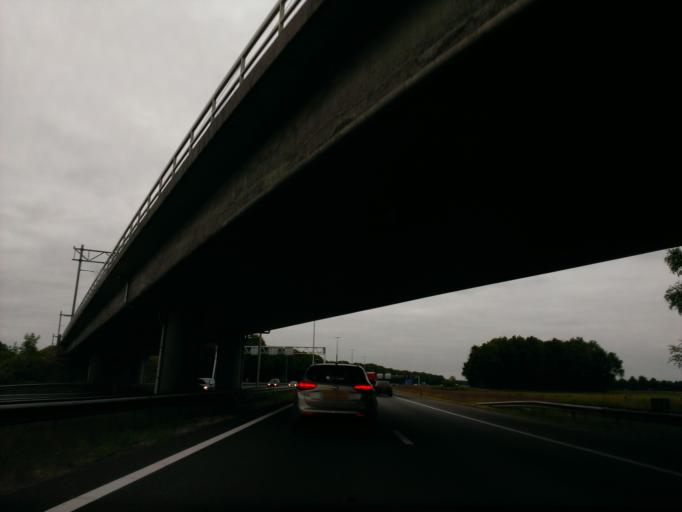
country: NL
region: Overijssel
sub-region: Gemeente Staphorst
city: Staphorst
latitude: 52.6689
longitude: 6.1992
